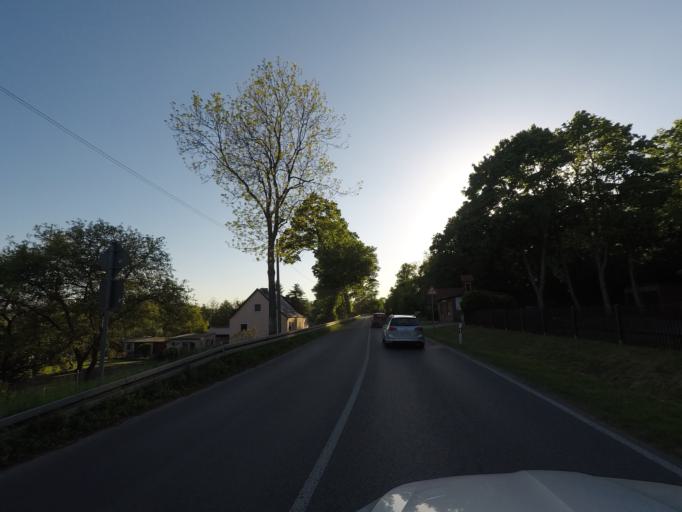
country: DE
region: Brandenburg
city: Bad Freienwalde
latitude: 52.8072
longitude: 14.0440
